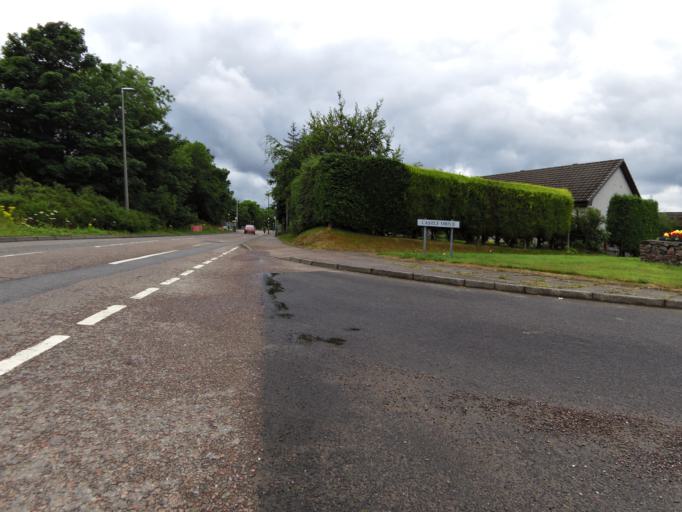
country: GB
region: Scotland
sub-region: Highland
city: Fort William
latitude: 56.8339
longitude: -5.0861
